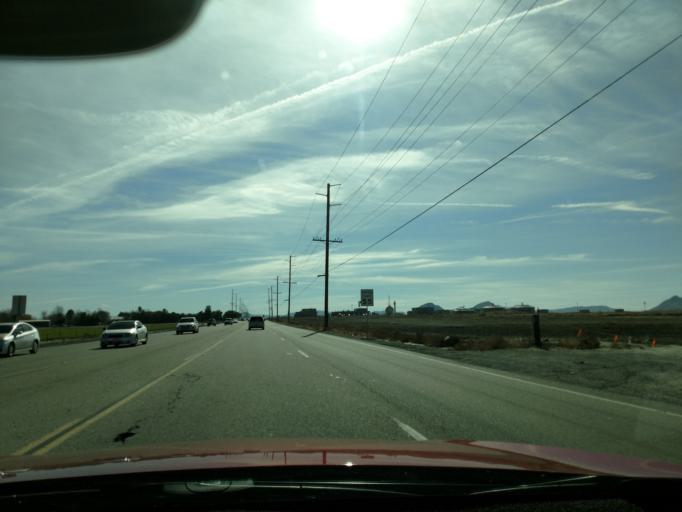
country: US
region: California
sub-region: Riverside County
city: San Jacinto
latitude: 33.8050
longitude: -117.0070
